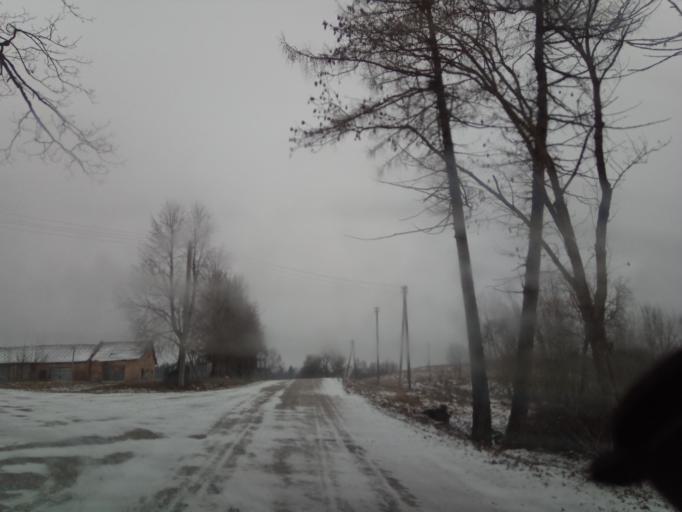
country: LT
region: Utenos apskritis
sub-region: Anyksciai
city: Anyksciai
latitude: 55.4241
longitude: 25.1122
